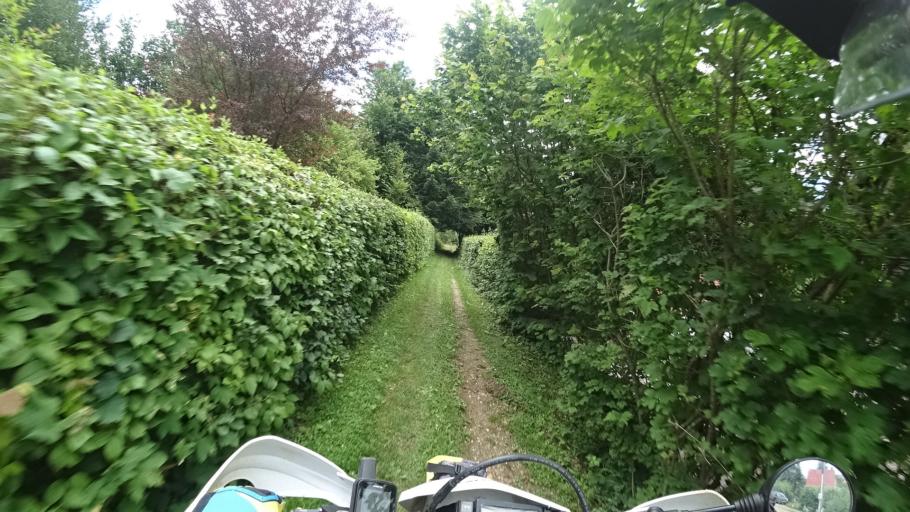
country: HR
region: Primorsko-Goranska
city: Hreljin
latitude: 45.3013
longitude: 14.7072
